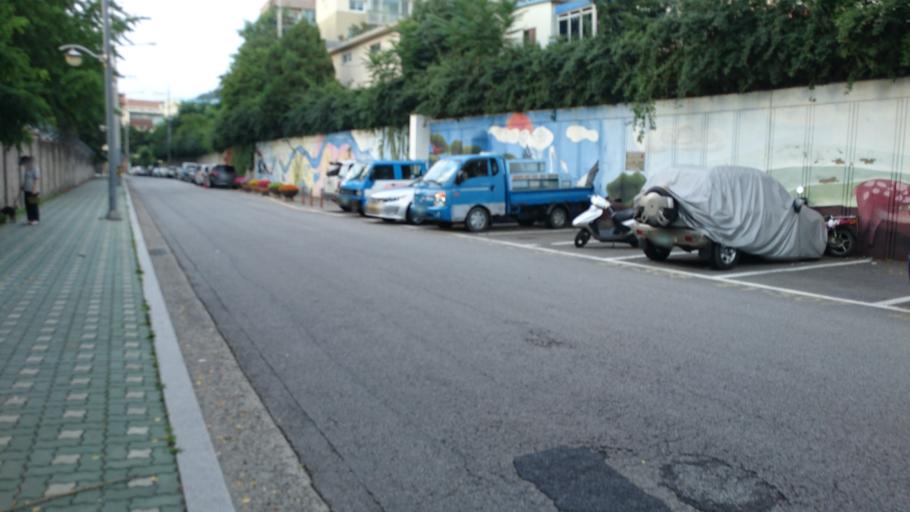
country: KR
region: Seoul
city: Seoul
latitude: 37.5432
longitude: 126.9792
